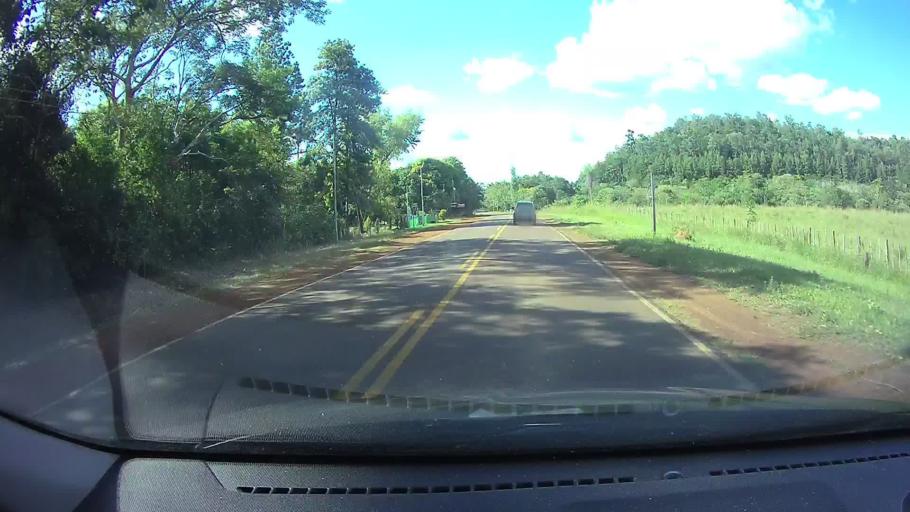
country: PY
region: Cordillera
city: Itacurubi de la Cordillera
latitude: -25.4805
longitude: -56.8806
